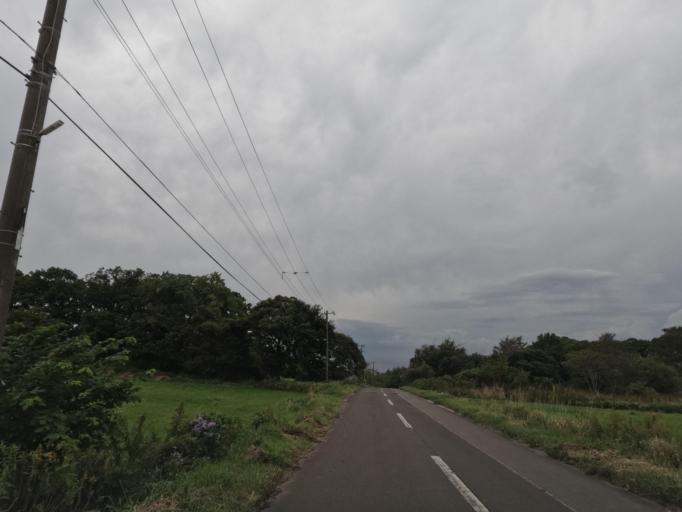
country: JP
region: Hokkaido
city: Date
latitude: 42.4057
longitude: 140.9187
